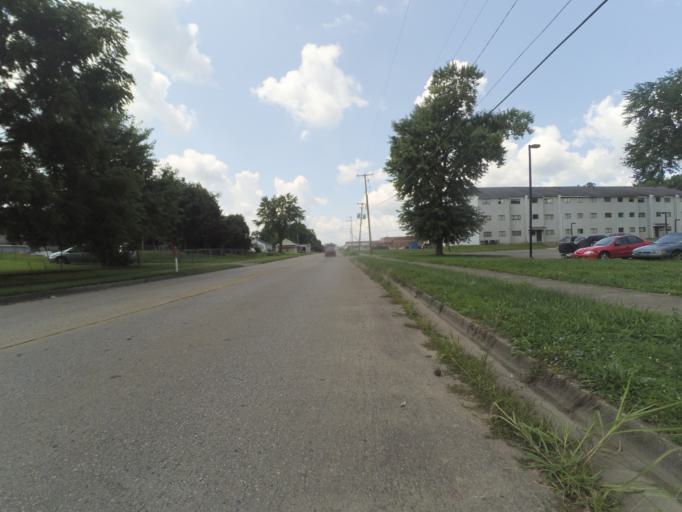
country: US
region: West Virginia
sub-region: Cabell County
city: Huntington
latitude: 38.4165
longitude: -82.4709
